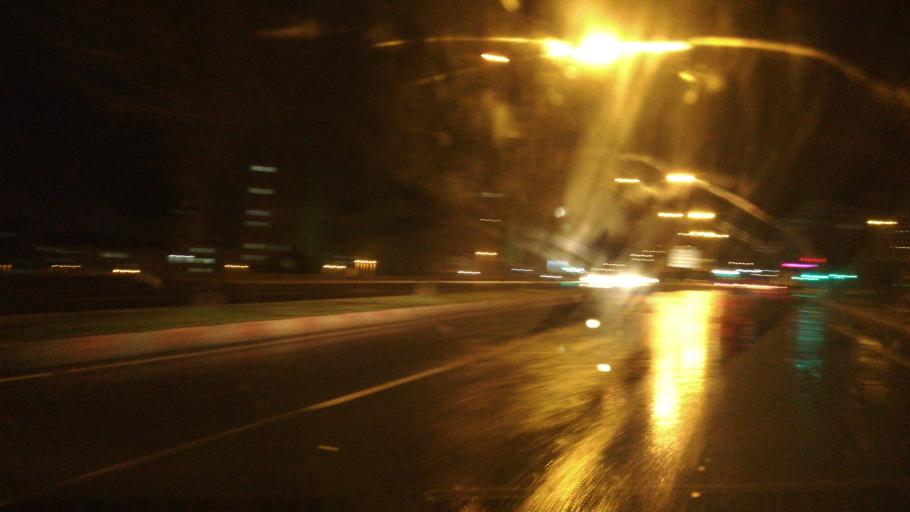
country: TR
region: Kahramanmaras
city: Kahramanmaras
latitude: 37.5948
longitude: 36.8927
